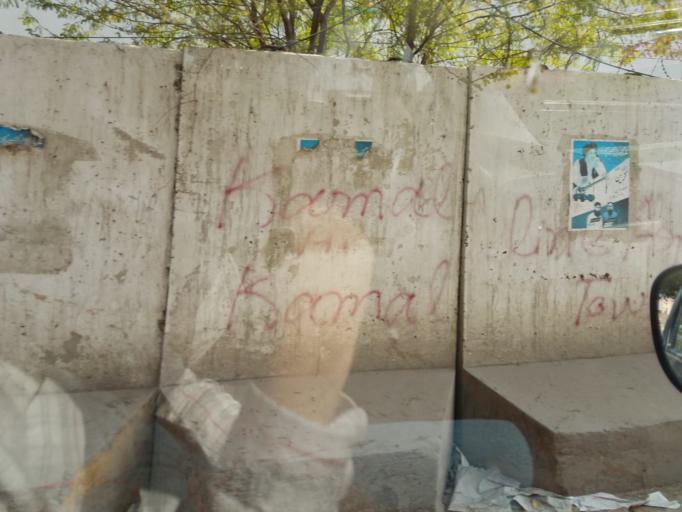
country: PK
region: Sindh
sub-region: Karachi District
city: Karachi
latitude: 24.8899
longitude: 67.0521
